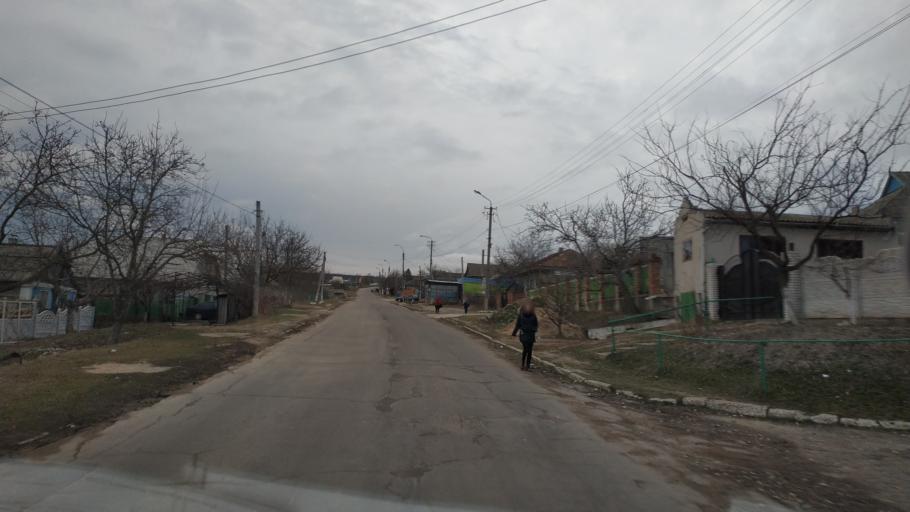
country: MD
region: Causeni
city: Causeni
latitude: 46.6309
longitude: 29.4022
